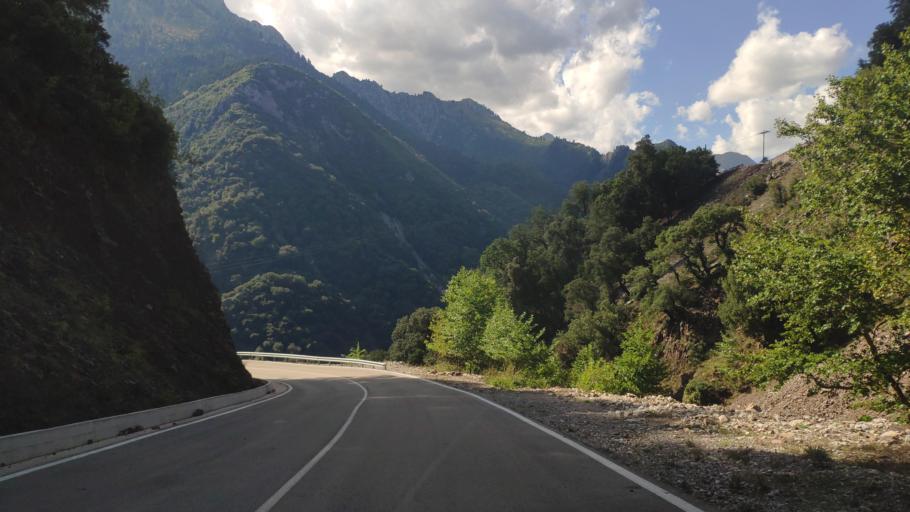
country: GR
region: Central Greece
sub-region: Nomos Evrytanias
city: Kerasochori
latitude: 39.1020
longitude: 21.6108
